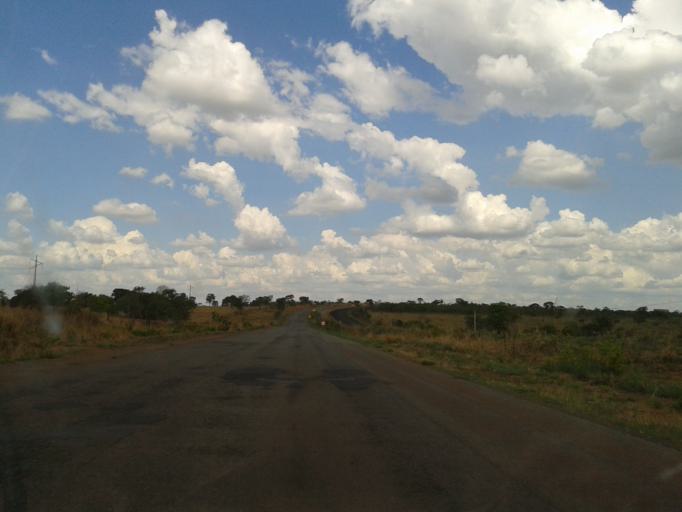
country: BR
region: Goias
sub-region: Caldas Novas
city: Caldas Novas
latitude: -17.6981
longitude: -48.7186
